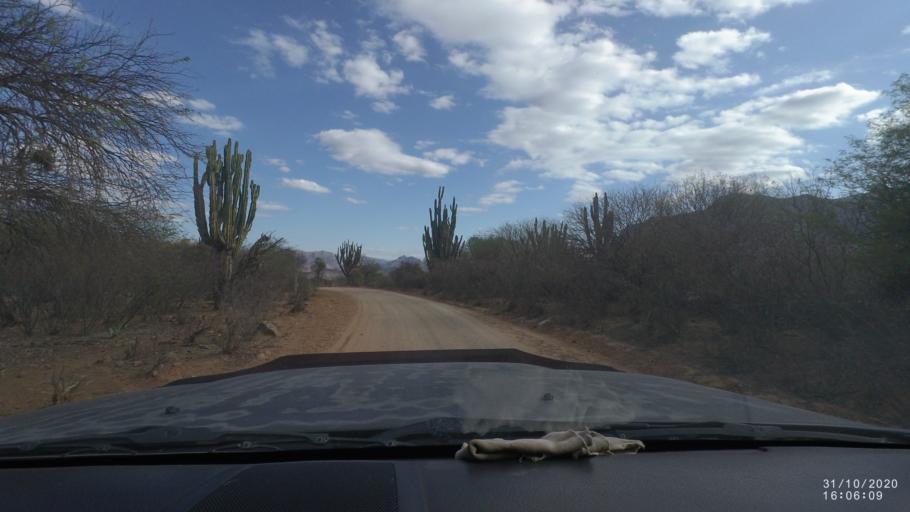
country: BO
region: Chuquisaca
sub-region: Provincia Zudanez
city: Mojocoya
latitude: -18.3715
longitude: -64.6486
